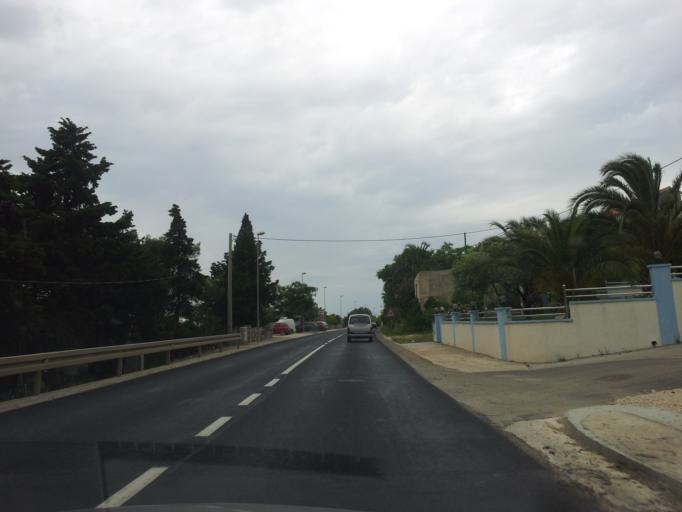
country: HR
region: Zadarska
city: Turanj
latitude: 43.9963
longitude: 15.3796
